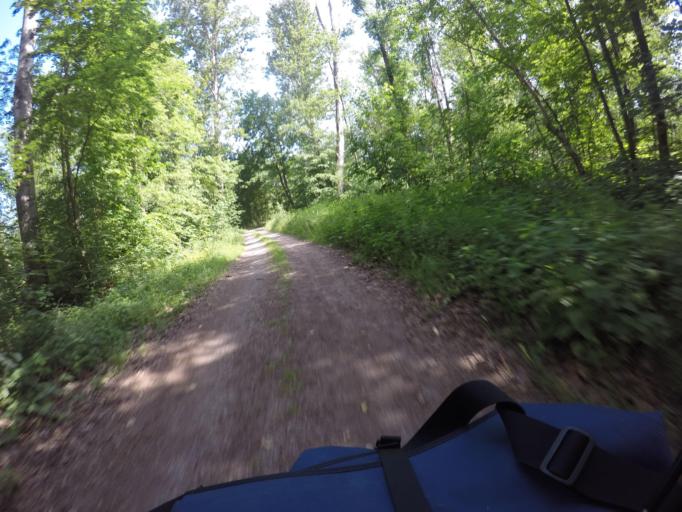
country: DE
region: Baden-Wuerttemberg
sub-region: Karlsruhe Region
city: Otigheim
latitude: 48.9077
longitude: 8.2325
